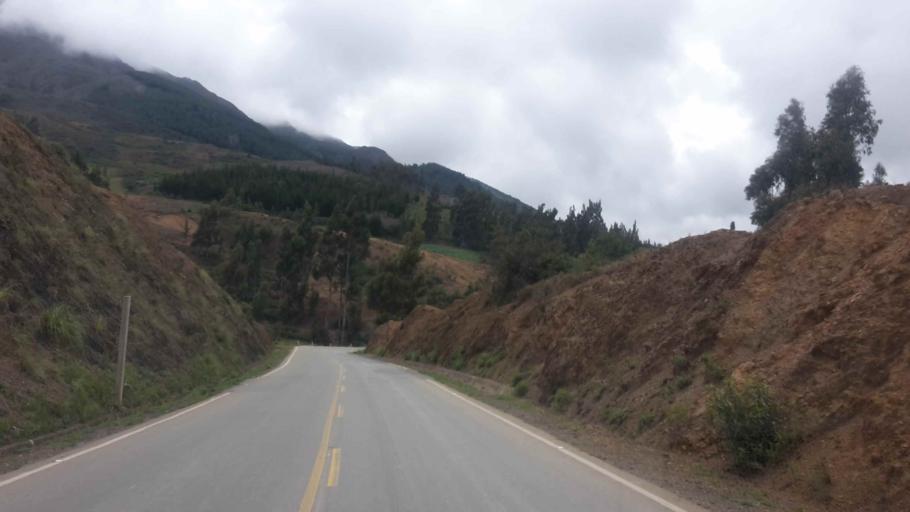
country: BO
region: Cochabamba
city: Totora
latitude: -17.5702
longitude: -65.3196
